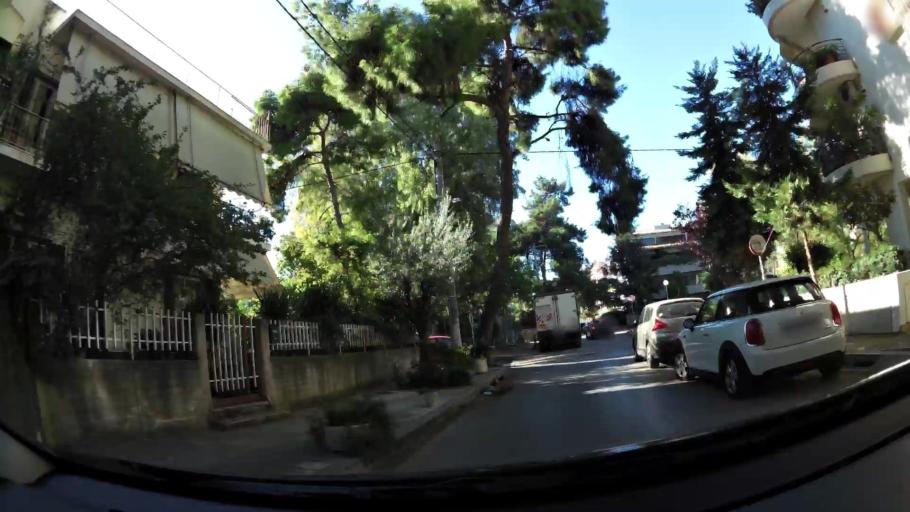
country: GR
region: Attica
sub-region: Nomarchia Athinas
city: Khalandrion
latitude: 38.0259
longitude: 23.7923
